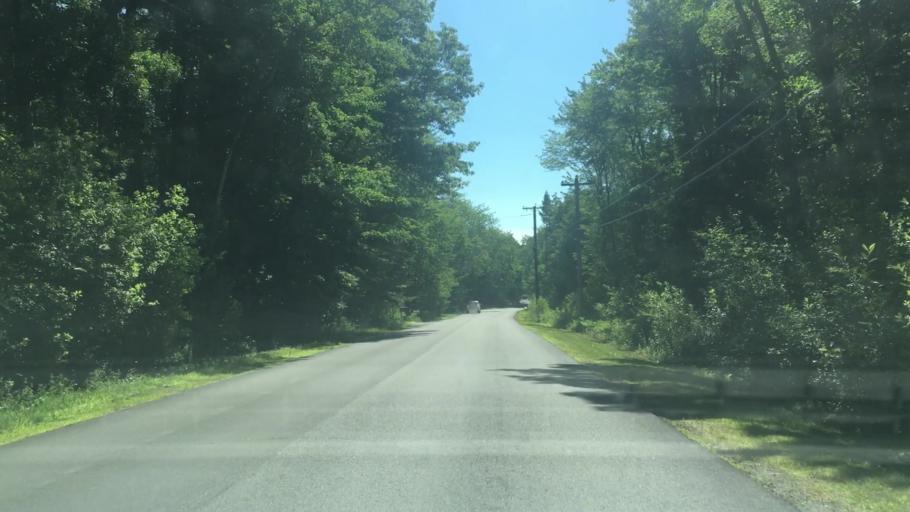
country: US
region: Maine
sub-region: Waldo County
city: Northport
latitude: 44.3819
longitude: -68.9777
